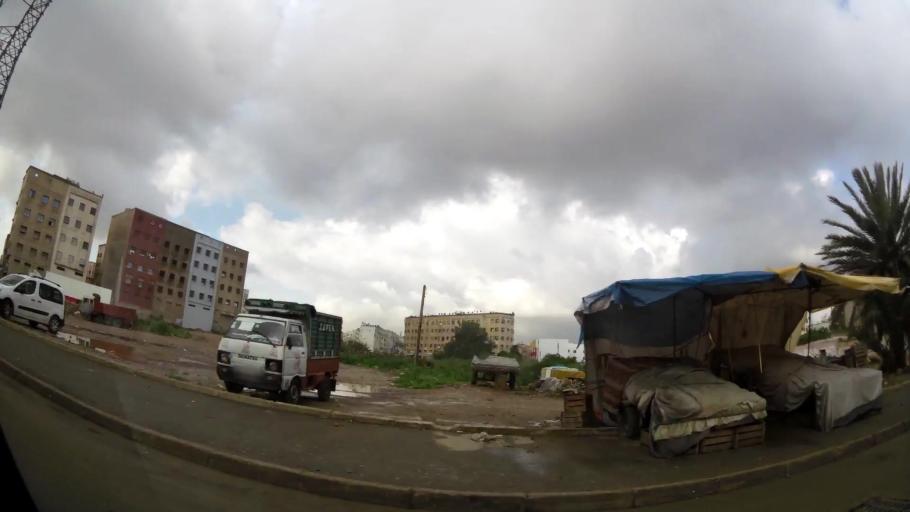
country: MA
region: Grand Casablanca
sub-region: Mediouna
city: Tit Mellil
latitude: 33.5885
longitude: -7.5247
